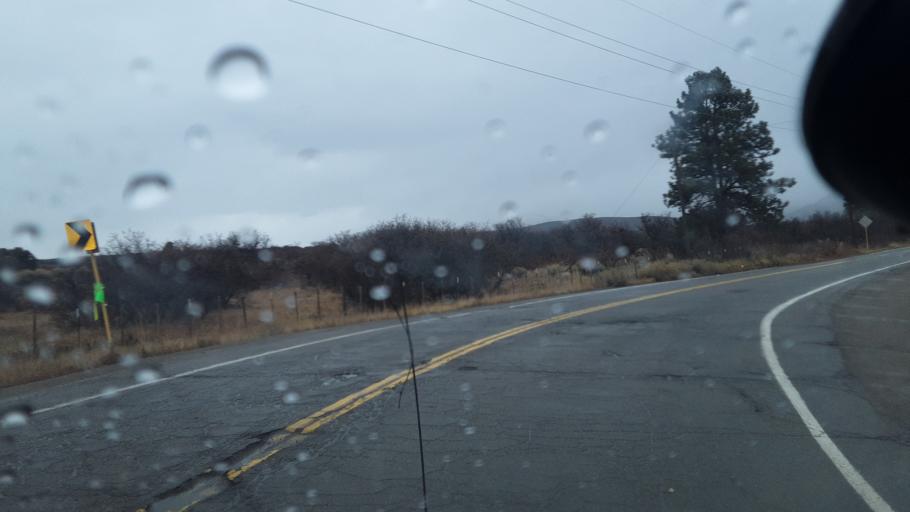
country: US
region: Colorado
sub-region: La Plata County
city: Durango
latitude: 37.2503
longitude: -108.0357
